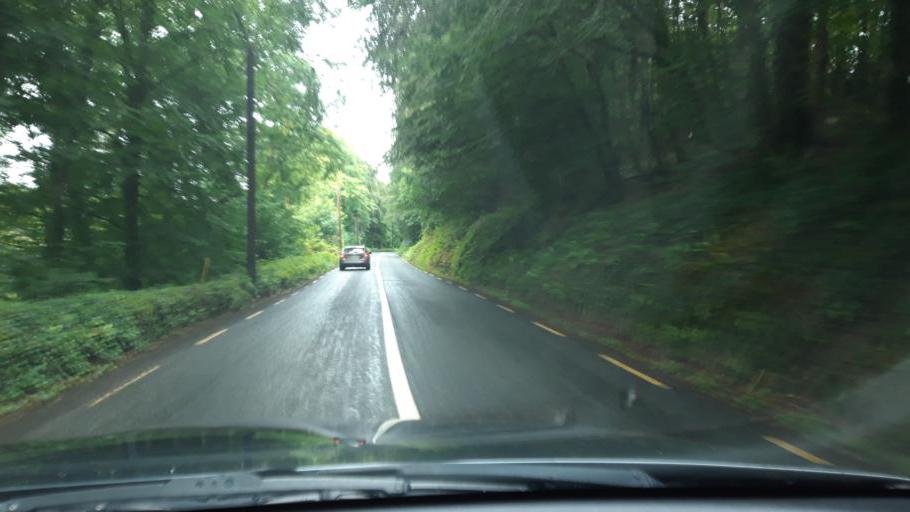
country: IE
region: Munster
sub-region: County Cork
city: Youghal
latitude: 52.1527
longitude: -7.8299
